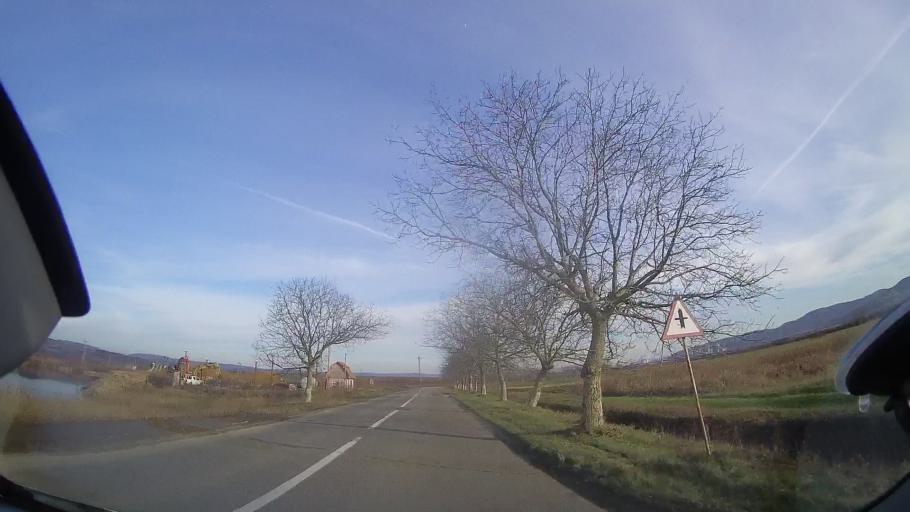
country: RO
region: Bihor
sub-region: Comuna Tetchea
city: Hotar
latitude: 47.0531
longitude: 22.2906
